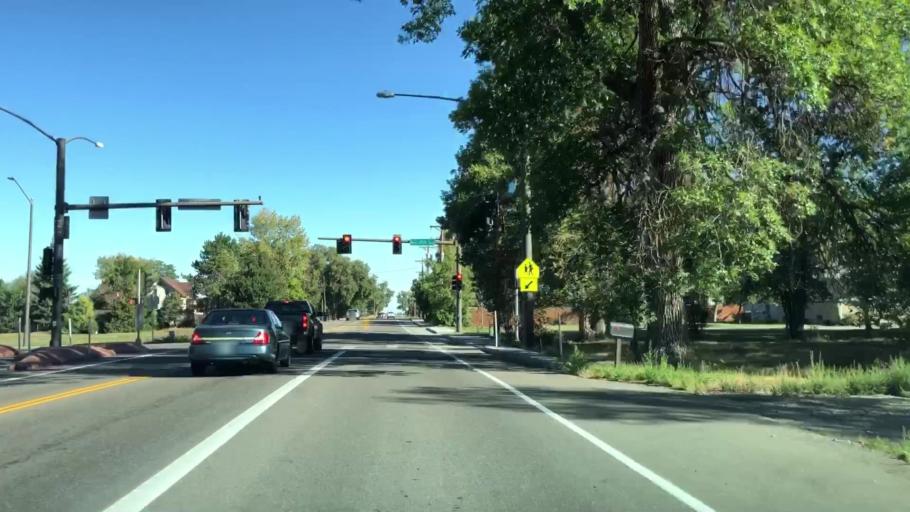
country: US
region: Colorado
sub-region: Larimer County
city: Loveland
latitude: 40.4215
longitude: -105.0586
